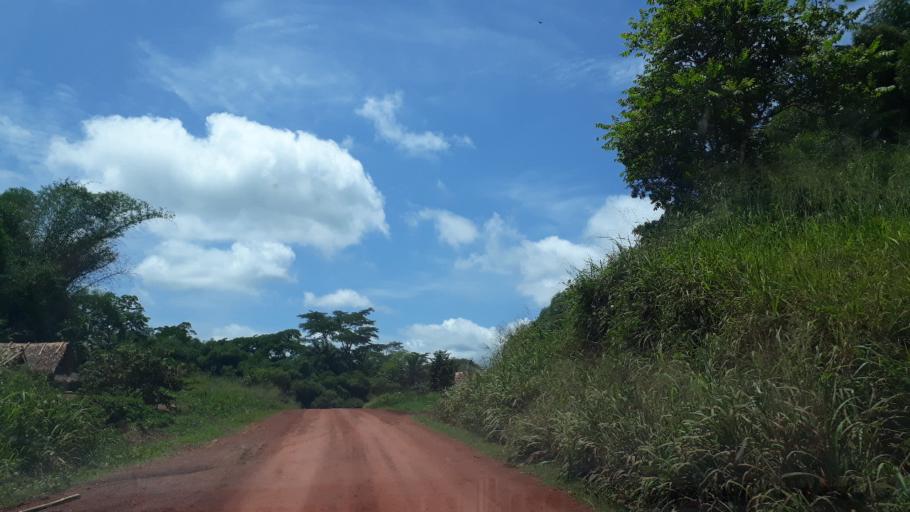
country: CD
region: Eastern Province
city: Kisangani
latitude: 0.5434
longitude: 25.9095
